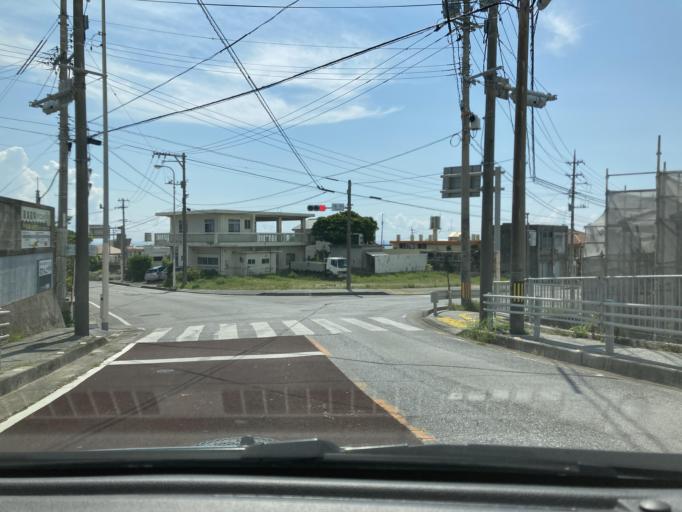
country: JP
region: Okinawa
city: Tomigusuku
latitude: 26.1431
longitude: 127.7924
